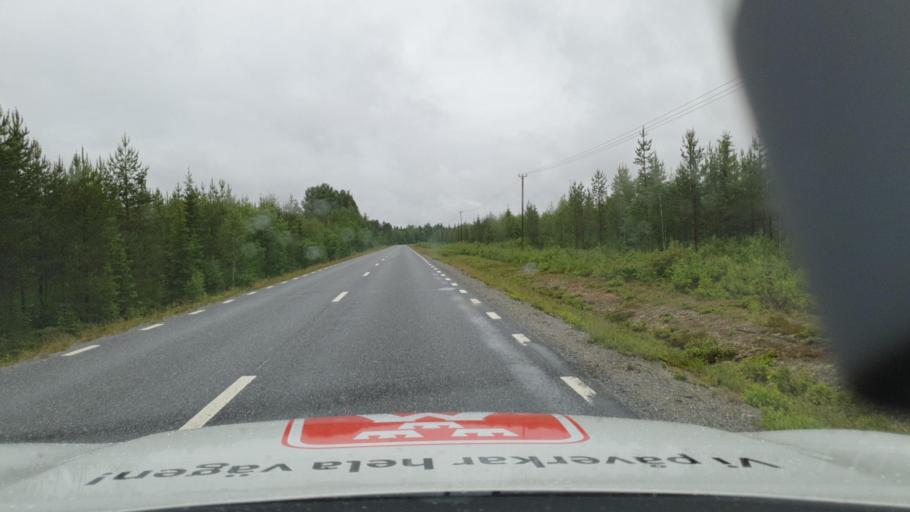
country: SE
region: Vaesterbotten
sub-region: Asele Kommun
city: Asele
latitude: 63.9643
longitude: 17.2665
